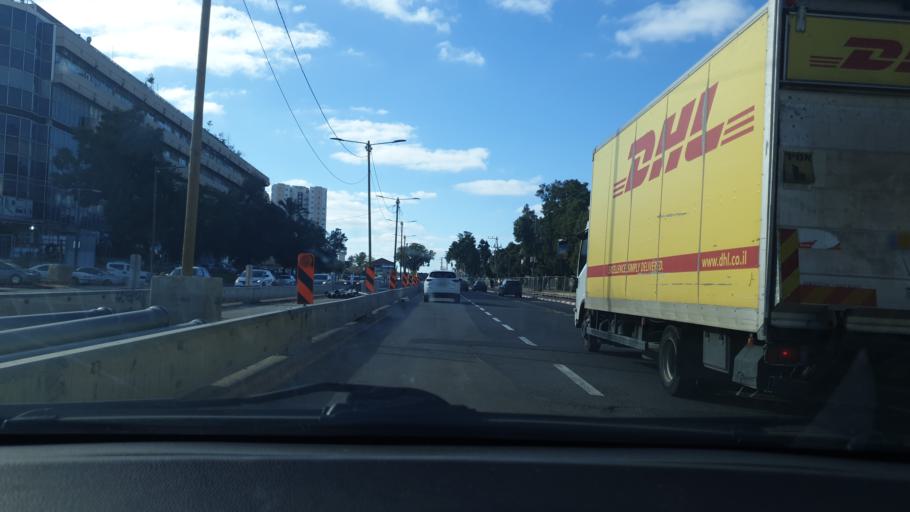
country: IL
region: Tel Aviv
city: Yafo
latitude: 32.0413
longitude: 34.7738
